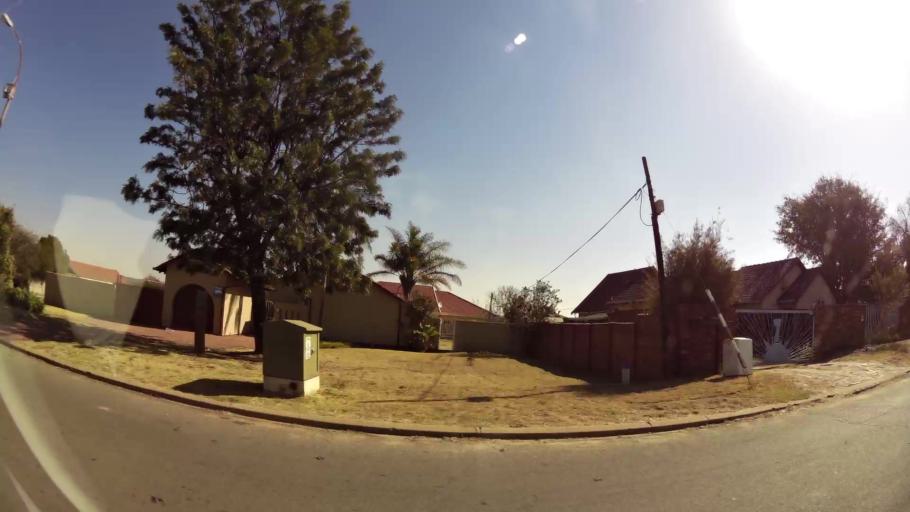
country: ZA
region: Gauteng
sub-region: Ekurhuleni Metropolitan Municipality
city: Tembisa
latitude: -26.0350
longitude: 28.2318
